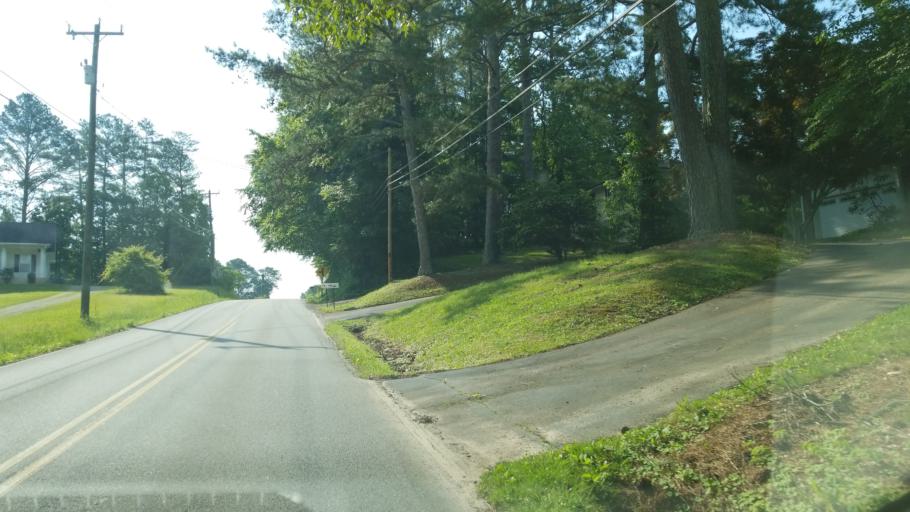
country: US
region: Tennessee
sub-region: Hamilton County
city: Collegedale
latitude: 35.0600
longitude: -85.0196
